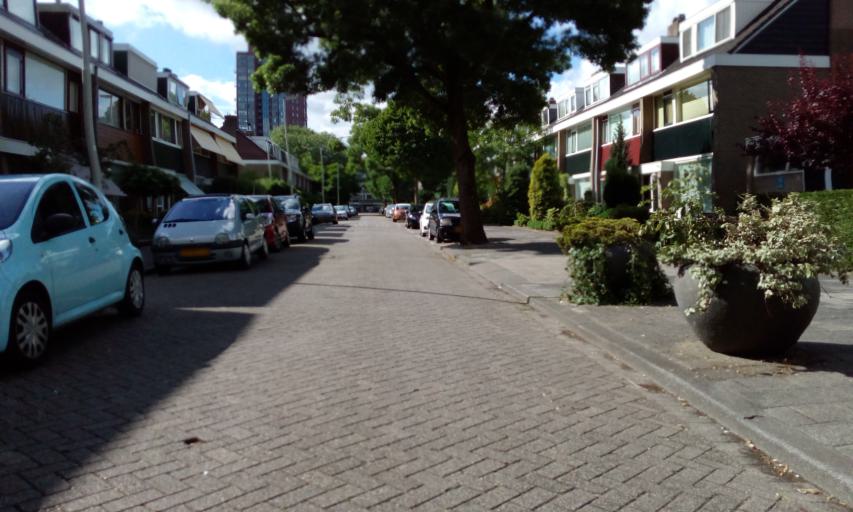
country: NL
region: South Holland
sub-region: Gemeente Rotterdam
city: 's-Gravenland
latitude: 51.9407
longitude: 4.5416
